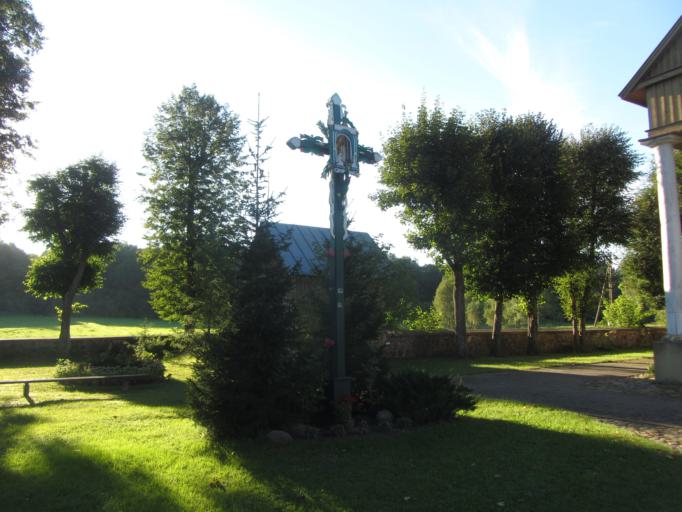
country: LT
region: Alytaus apskritis
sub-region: Alytus
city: Alytus
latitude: 54.4662
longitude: 24.0544
